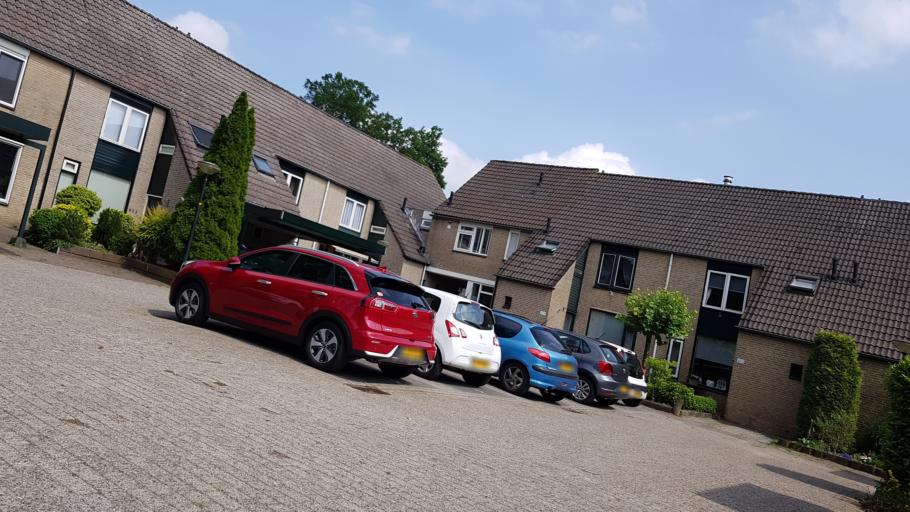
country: NL
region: Gelderland
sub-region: Gemeente Apeldoorn
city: Apeldoorn
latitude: 52.1904
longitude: 5.9999
